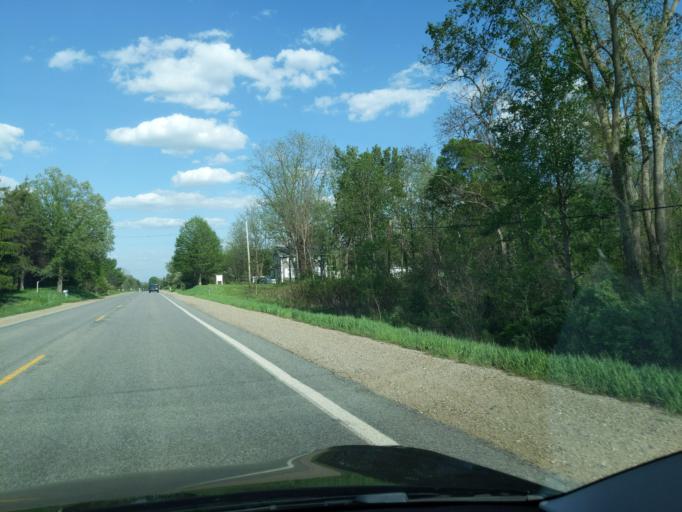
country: US
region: Michigan
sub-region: Eaton County
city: Grand Ledge
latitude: 42.7555
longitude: -84.7870
